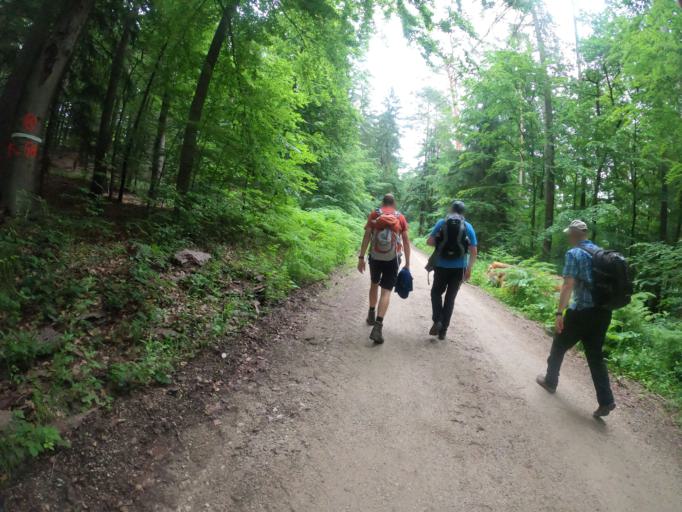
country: DE
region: Bavaria
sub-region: Upper Franconia
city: Litzendorf
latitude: 49.9263
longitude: 11.0239
